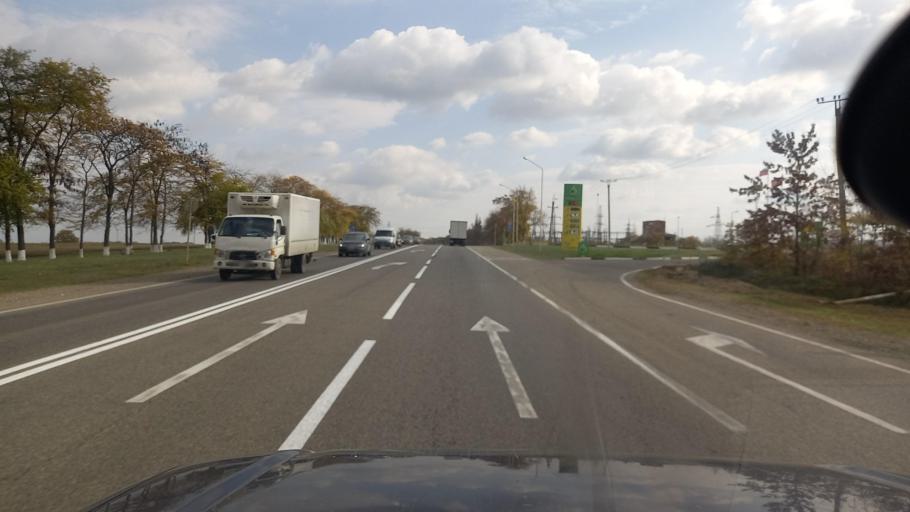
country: RU
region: Krasnodarskiy
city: Kholmskiy
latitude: 44.8479
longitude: 38.4179
